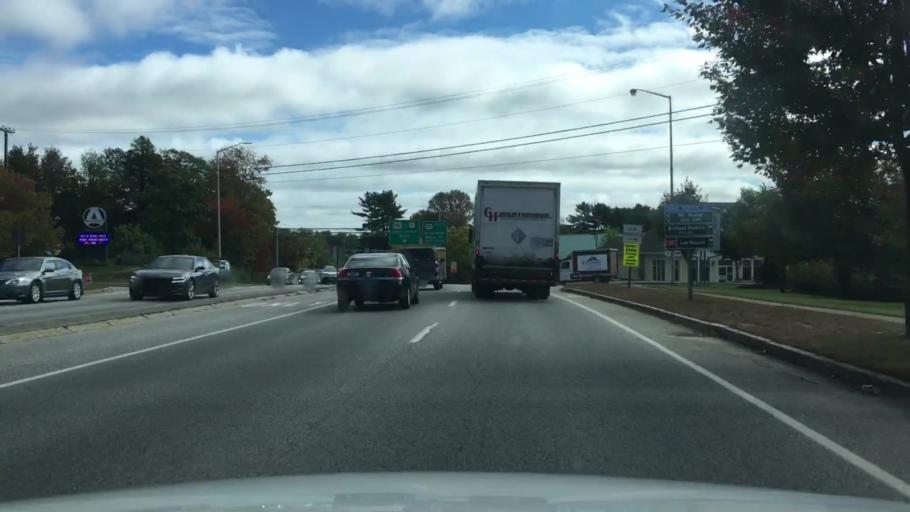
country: US
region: Maine
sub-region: Sagadahoc County
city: Topsham
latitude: 43.9373
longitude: -69.9702
